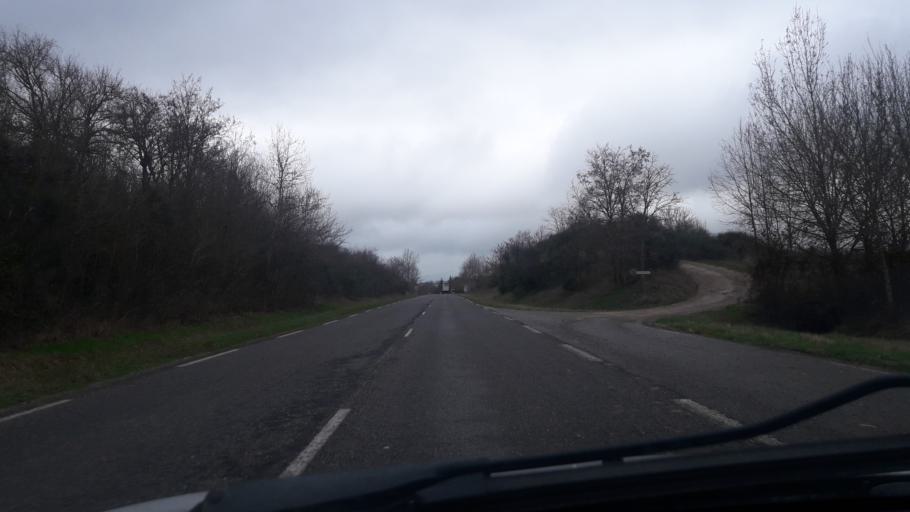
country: FR
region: Midi-Pyrenees
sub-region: Departement du Gers
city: Gimont
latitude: 43.6803
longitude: 1.0073
